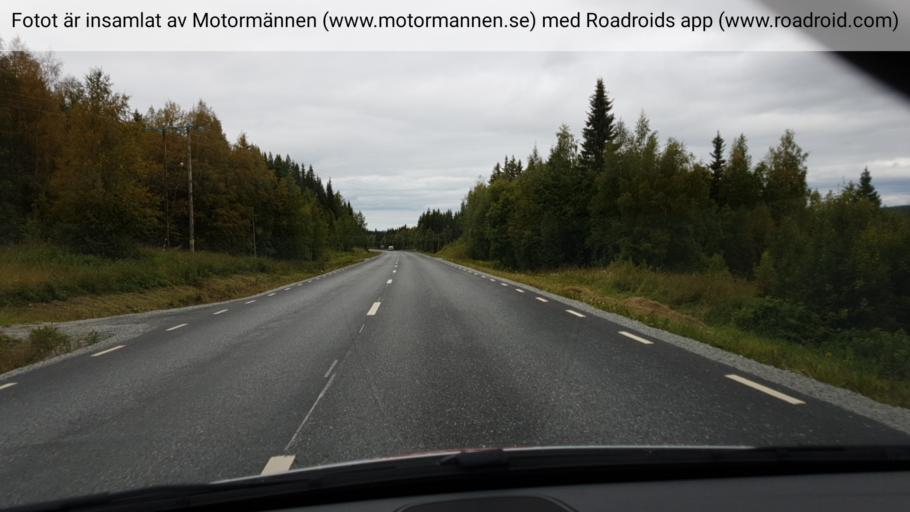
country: SE
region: Jaemtland
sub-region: Stroemsunds Kommun
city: Stroemsund
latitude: 64.2193
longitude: 15.5462
